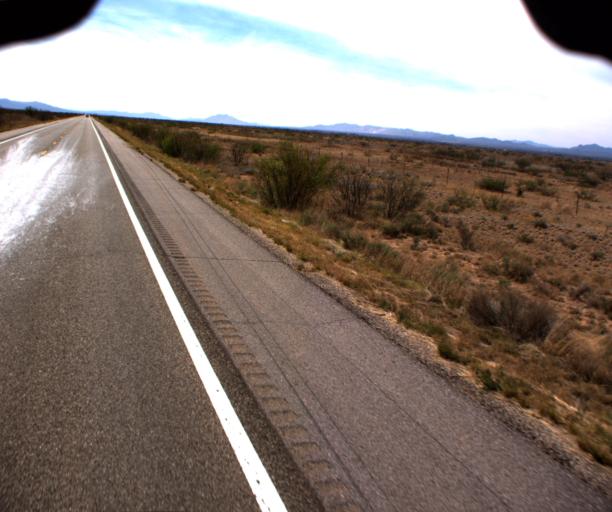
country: US
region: Arizona
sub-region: Cochise County
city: Pirtleville
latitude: 31.5099
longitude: -109.6403
